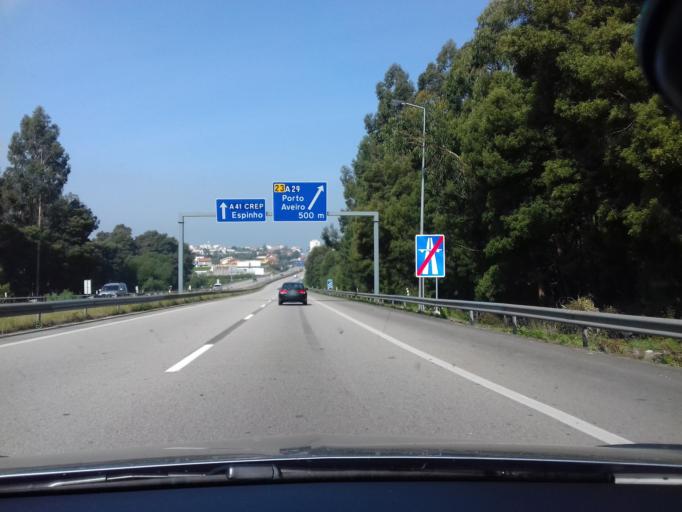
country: PT
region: Aveiro
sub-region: Santa Maria da Feira
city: Nogueira da Regedoura
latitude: 41.0085
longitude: -8.6095
